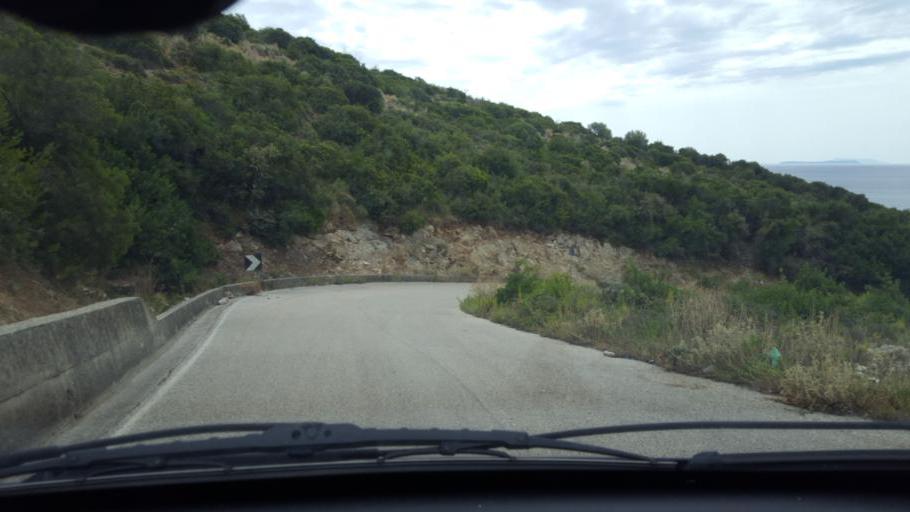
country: AL
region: Vlore
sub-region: Rrethi i Sarandes
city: Lukove
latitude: 39.9752
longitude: 19.9168
